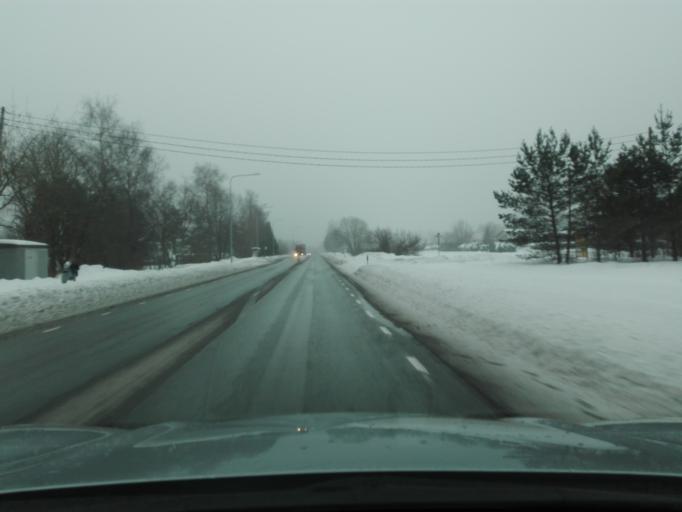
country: EE
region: Harju
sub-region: Kiili vald
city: Kiili
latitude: 59.3409
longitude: 24.7739
